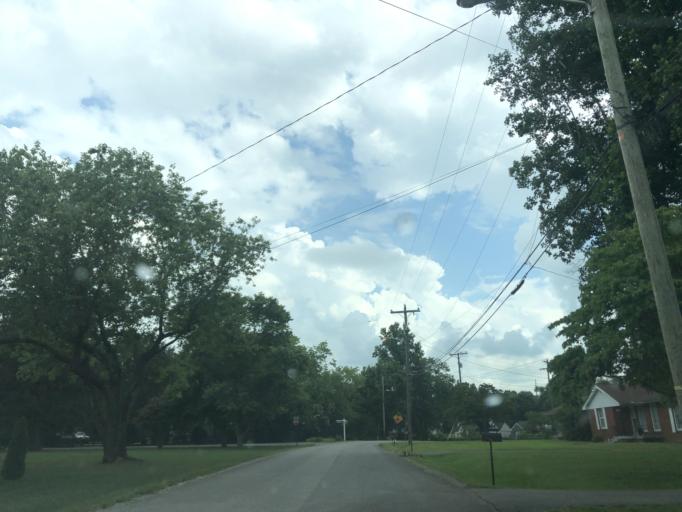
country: US
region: Tennessee
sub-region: Davidson County
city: Lakewood
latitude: 36.1660
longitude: -86.6691
